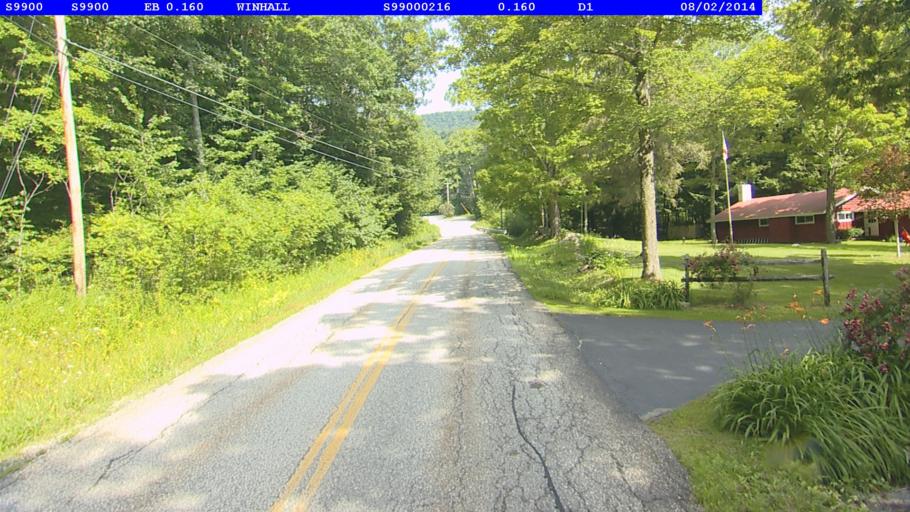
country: US
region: Vermont
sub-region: Bennington County
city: Manchester Center
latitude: 43.1942
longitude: -72.9990
